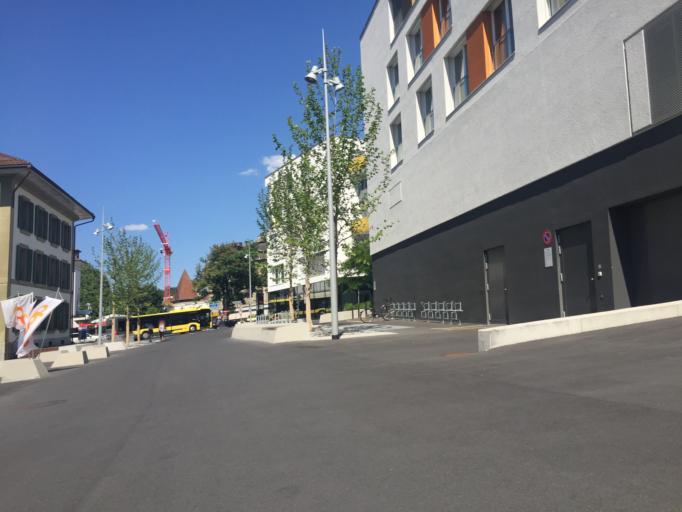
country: CH
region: Bern
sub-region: Thun District
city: Thun
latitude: 46.7589
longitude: 7.6248
